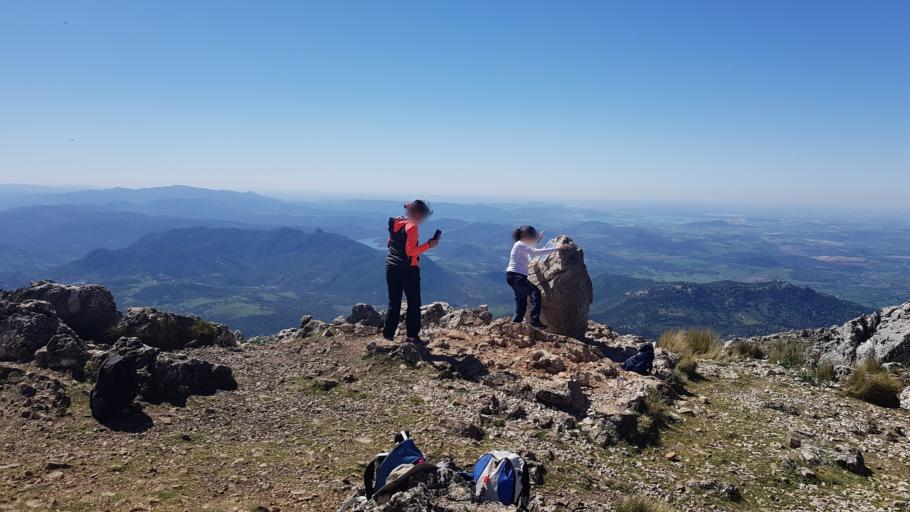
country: ES
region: Andalusia
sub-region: Provincia de Cadiz
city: Grazalema
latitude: 36.7657
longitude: -5.4224
